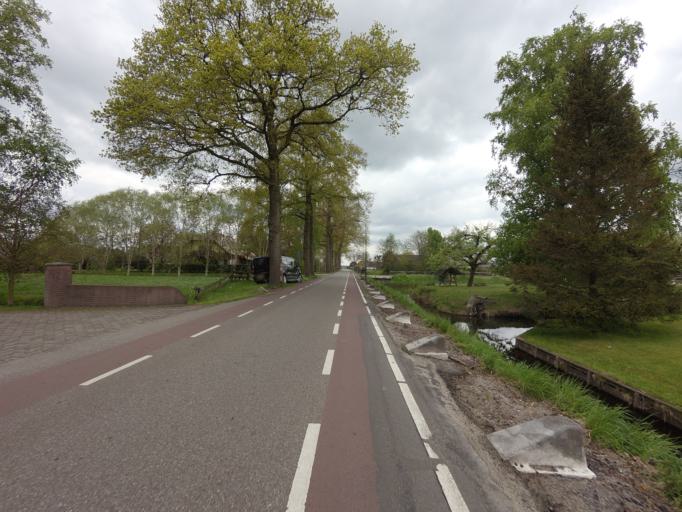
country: NL
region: Utrecht
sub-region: Gemeente De Bilt
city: De Bilt
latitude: 52.1507
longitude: 5.1518
